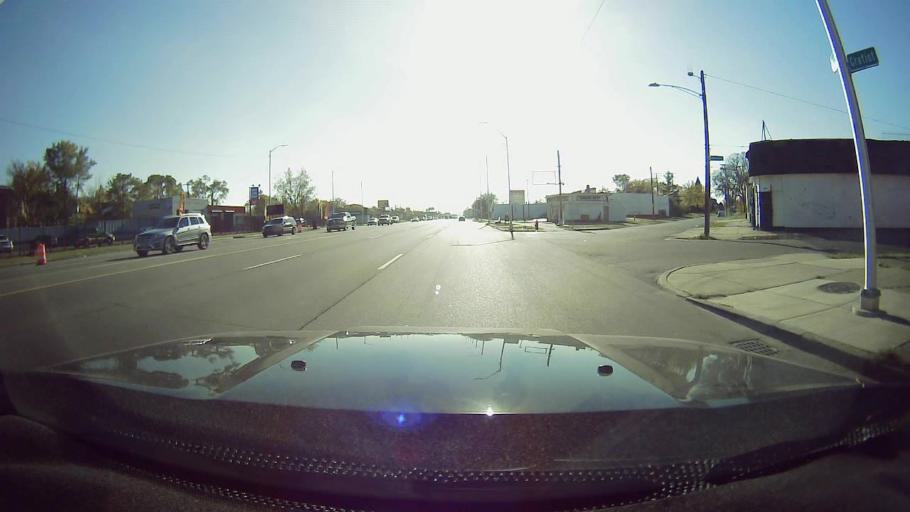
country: US
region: Michigan
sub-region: Wayne County
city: Hamtramck
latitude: 42.4115
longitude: -82.9933
